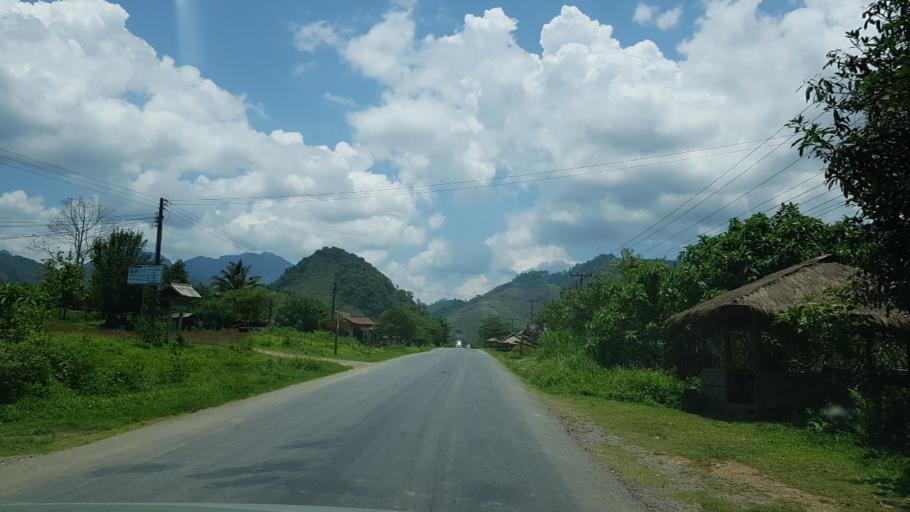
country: LA
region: Vientiane
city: Muang Kasi
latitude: 19.1289
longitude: 102.2669
